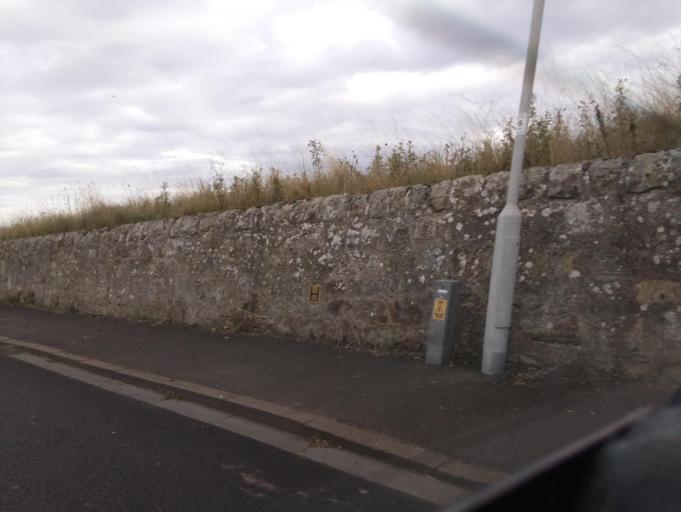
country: GB
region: Scotland
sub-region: Fife
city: Saint Andrews
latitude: 56.3319
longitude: -2.7833
